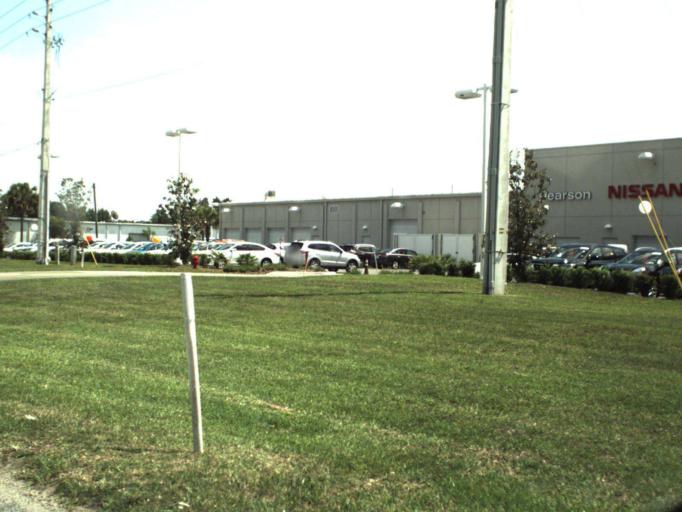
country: US
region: Florida
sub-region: Marion County
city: Ocala
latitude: 29.1729
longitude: -82.1596
